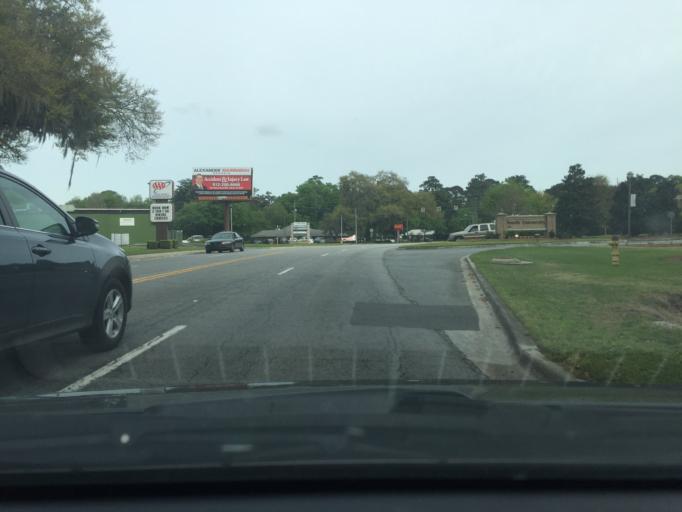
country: US
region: Georgia
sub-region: Chatham County
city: Isle of Hope
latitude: 32.0005
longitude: -81.1053
